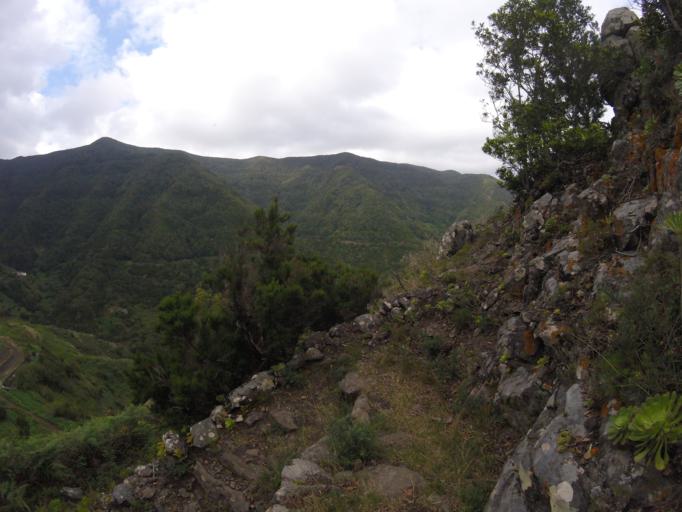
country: ES
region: Canary Islands
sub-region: Provincia de Santa Cruz de Tenerife
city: Tegueste
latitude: 28.5440
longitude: -16.2857
